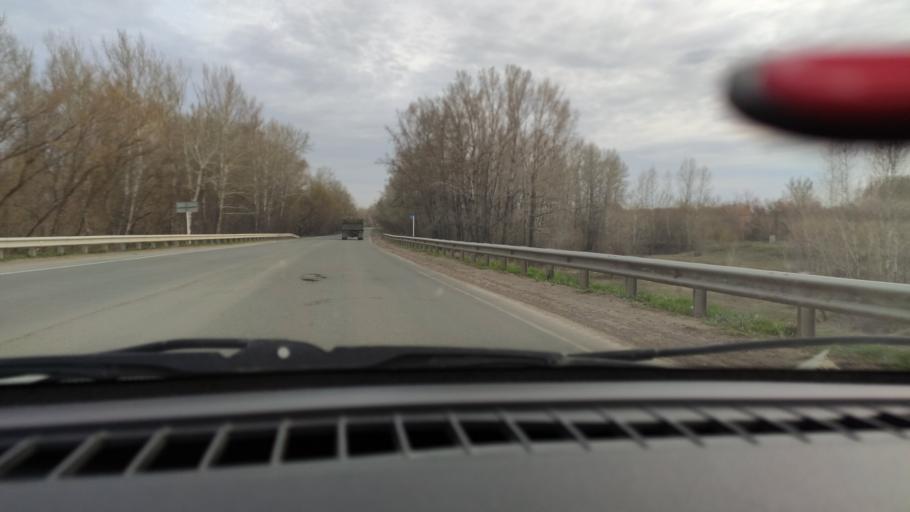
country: RU
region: Orenburg
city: Tatarskaya Kargala
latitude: 51.9370
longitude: 55.1753
